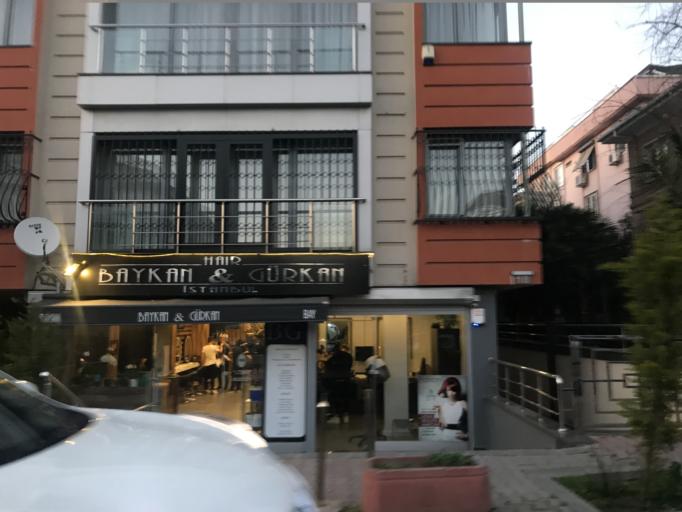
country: TR
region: Istanbul
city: Bahcelievler
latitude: 40.9613
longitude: 28.8229
